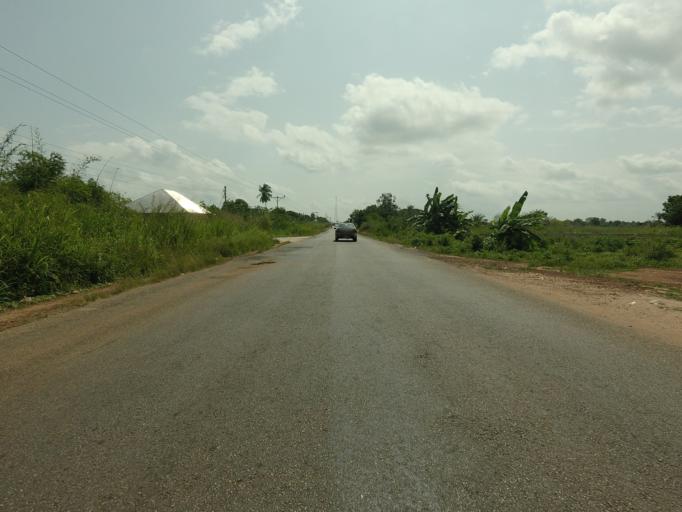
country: TG
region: Maritime
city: Lome
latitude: 6.2294
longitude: 1.0113
